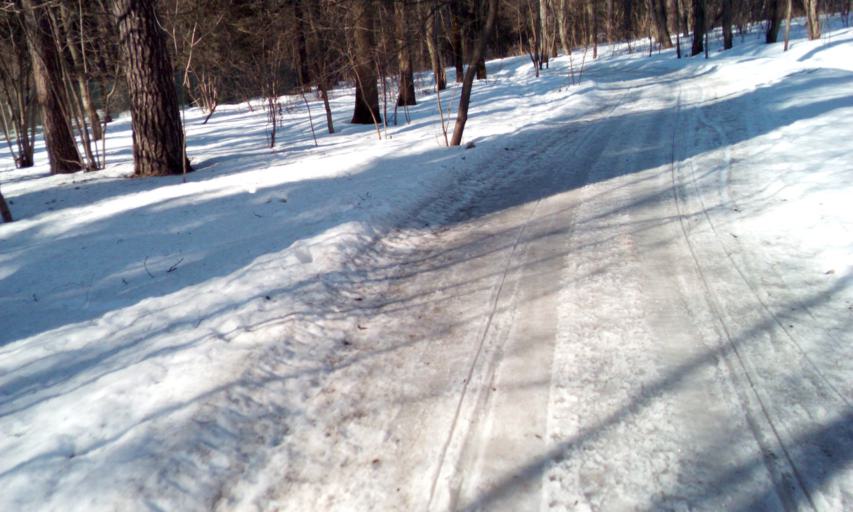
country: RU
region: Moscow
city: Novo-Peredelkino
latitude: 55.6651
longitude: 37.3478
